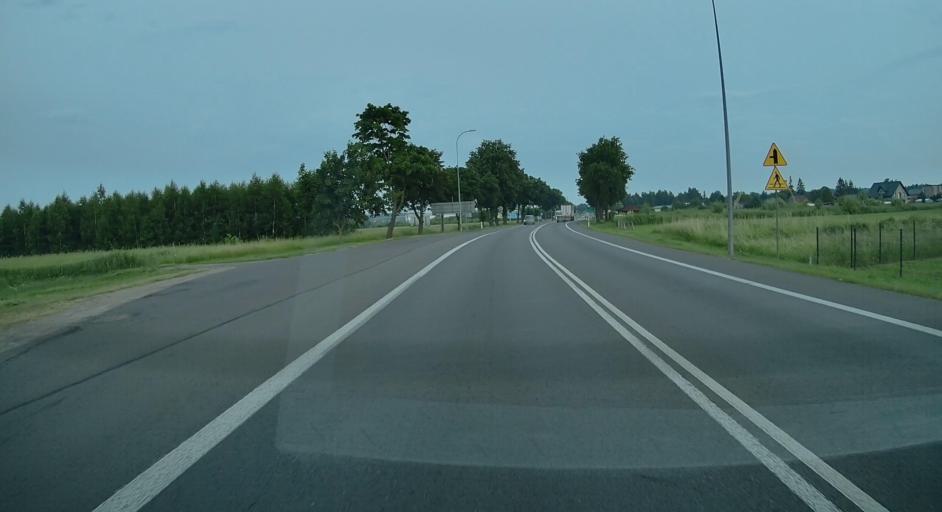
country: PL
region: Masovian Voivodeship
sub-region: Siedlce
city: Siedlce
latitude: 52.1316
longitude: 22.3304
